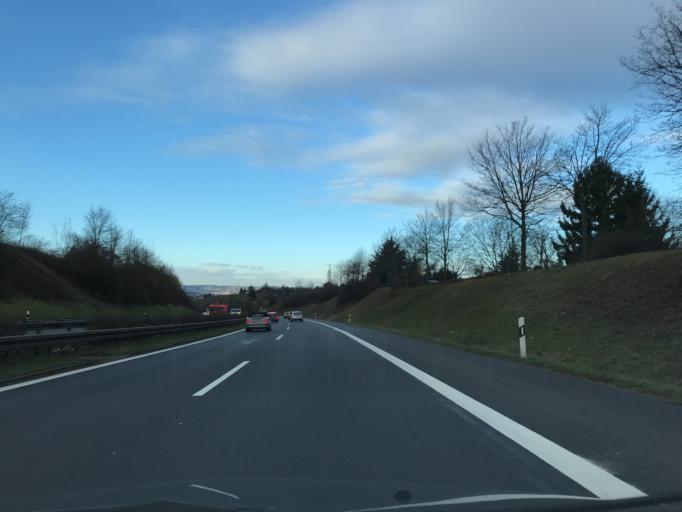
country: DE
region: Baden-Wuerttemberg
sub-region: Regierungsbezirk Stuttgart
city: Fellbach
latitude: 48.7989
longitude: 9.2637
